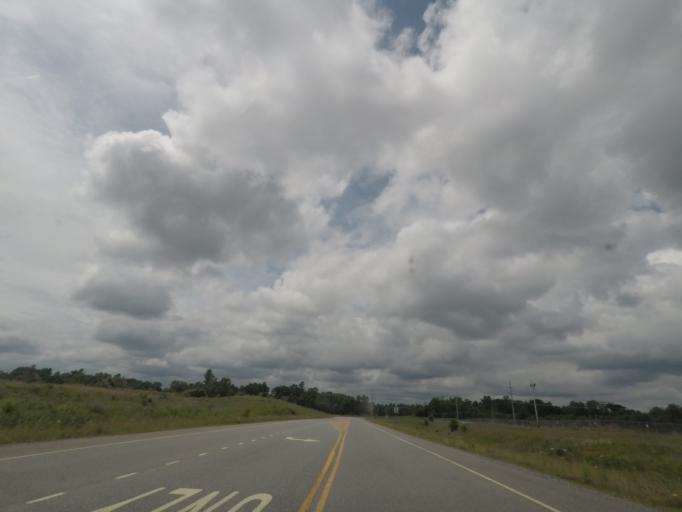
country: US
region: New York
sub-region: Saratoga County
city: Country Knolls
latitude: 42.9623
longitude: -73.7530
